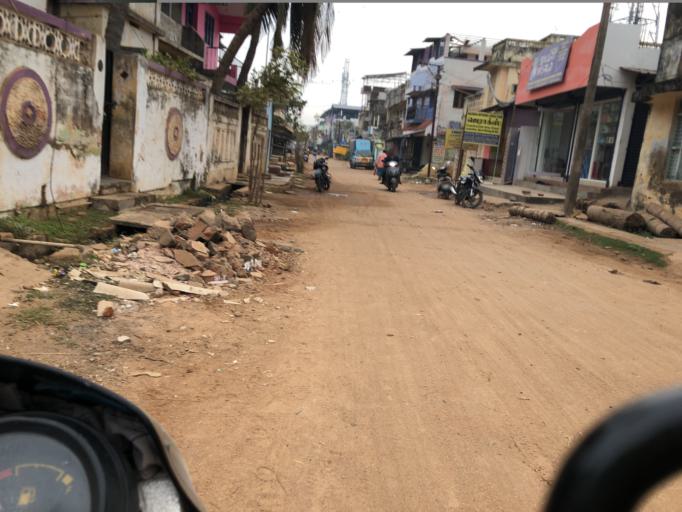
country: IN
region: Tamil Nadu
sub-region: Thanjavur
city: Adirampattinam
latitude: 10.3400
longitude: 79.3822
